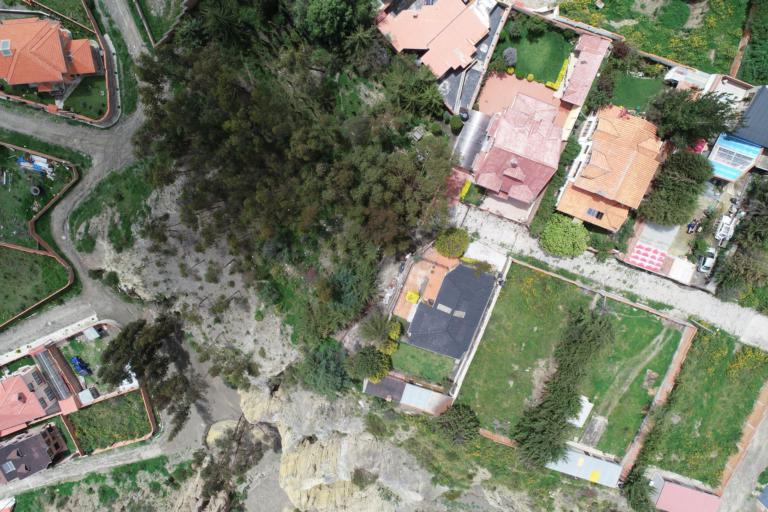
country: BO
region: La Paz
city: La Paz
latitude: -16.4982
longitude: -68.0817
